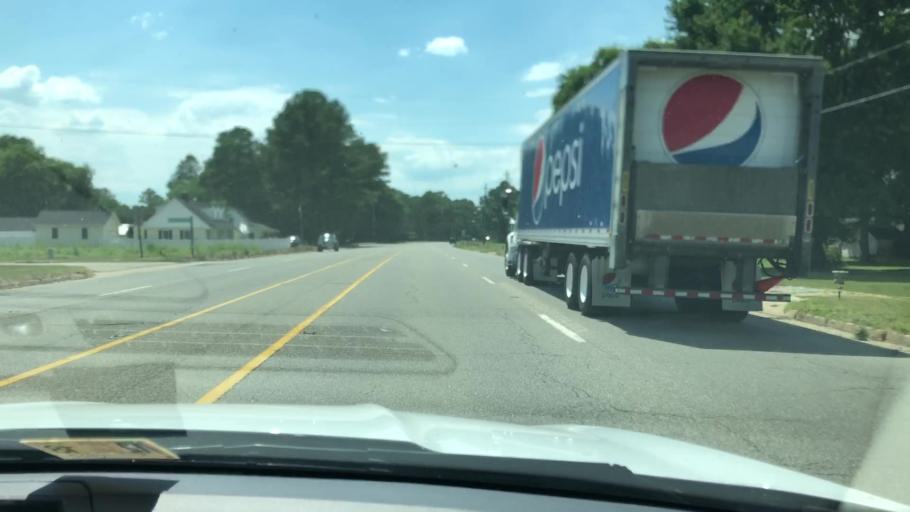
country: US
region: Virginia
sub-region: King William County
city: West Point
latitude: 37.5348
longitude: -76.7732
